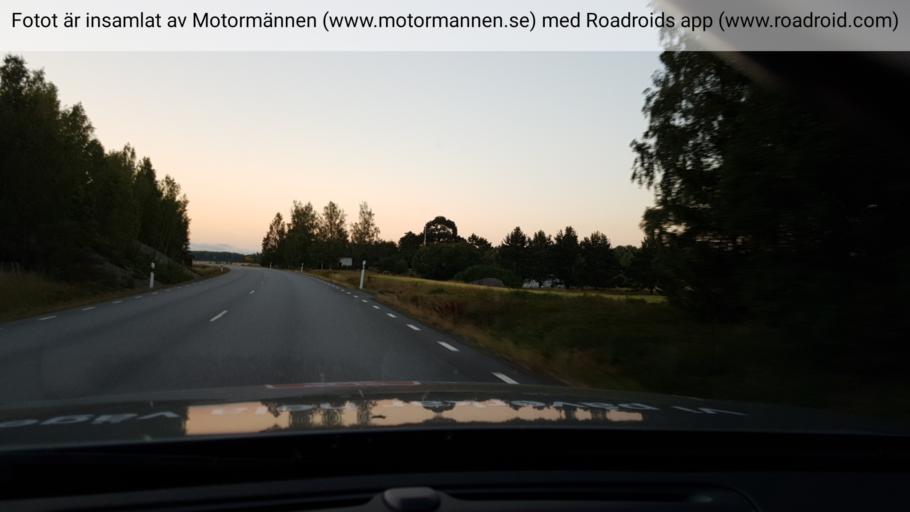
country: SE
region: Uppsala
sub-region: Heby Kommun
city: OEstervala
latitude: 60.1557
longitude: 17.2044
